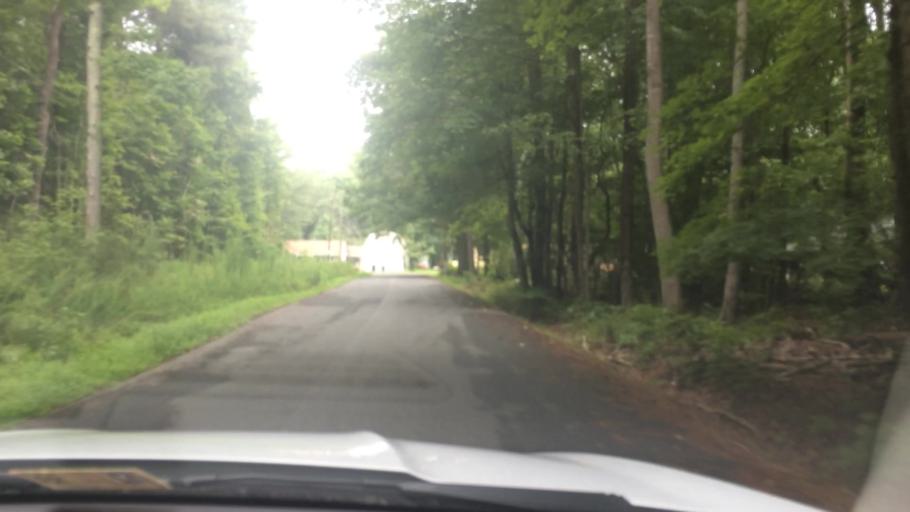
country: US
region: Virginia
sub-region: York County
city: Yorktown
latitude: 37.2232
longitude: -76.5416
